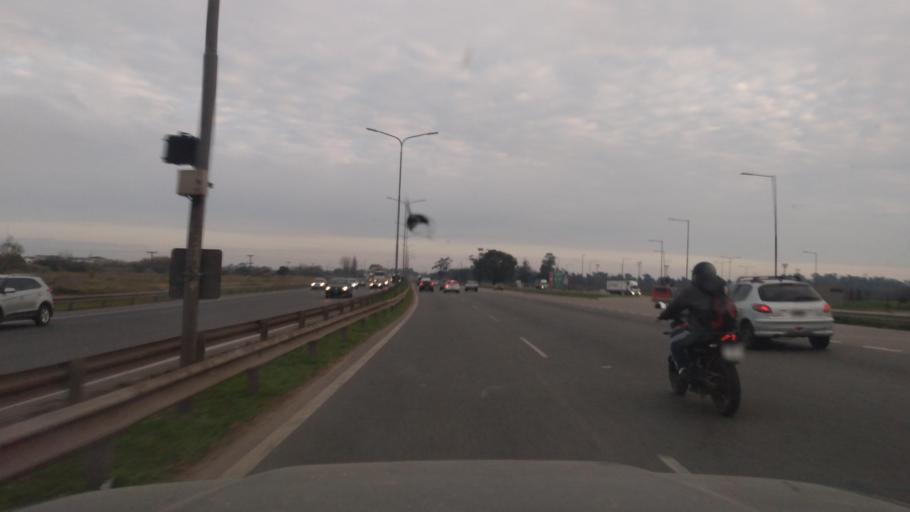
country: AR
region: Buenos Aires
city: Hurlingham
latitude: -34.5559
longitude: -58.6271
